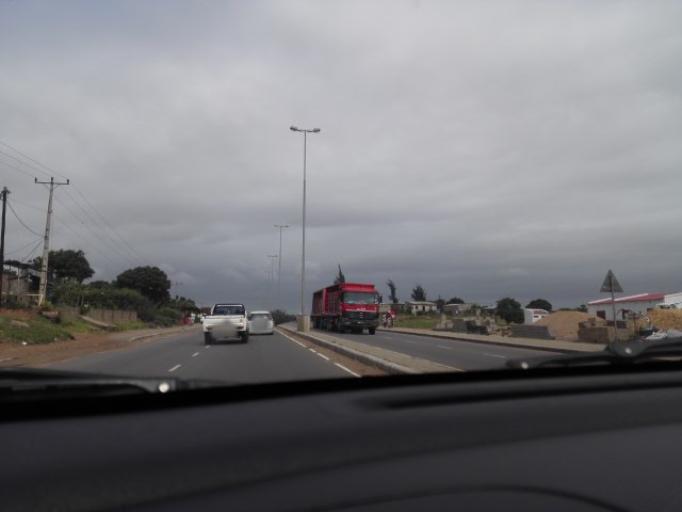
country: MZ
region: Maputo City
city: Maputo
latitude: -25.8240
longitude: 32.5934
